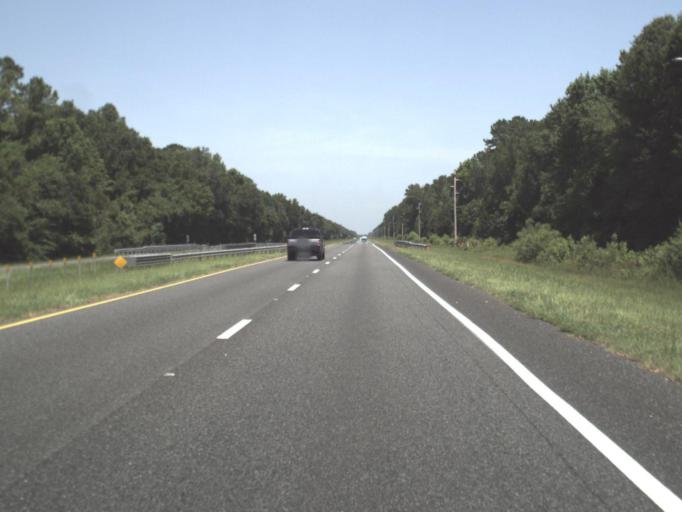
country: US
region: Florida
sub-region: Taylor County
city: Steinhatchee
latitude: 29.6887
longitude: -83.2699
